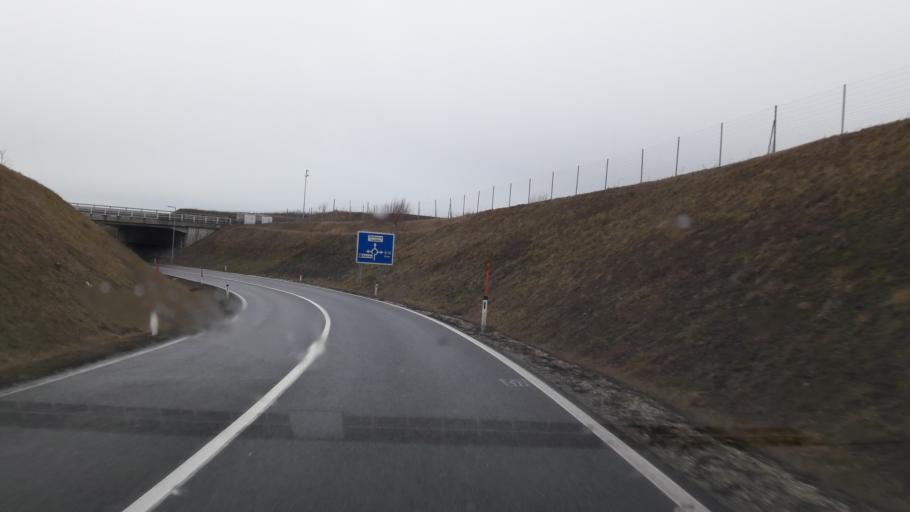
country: AT
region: Lower Austria
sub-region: Politischer Bezirk Mistelbach
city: Hochleithen
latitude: 48.4290
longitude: 16.5516
